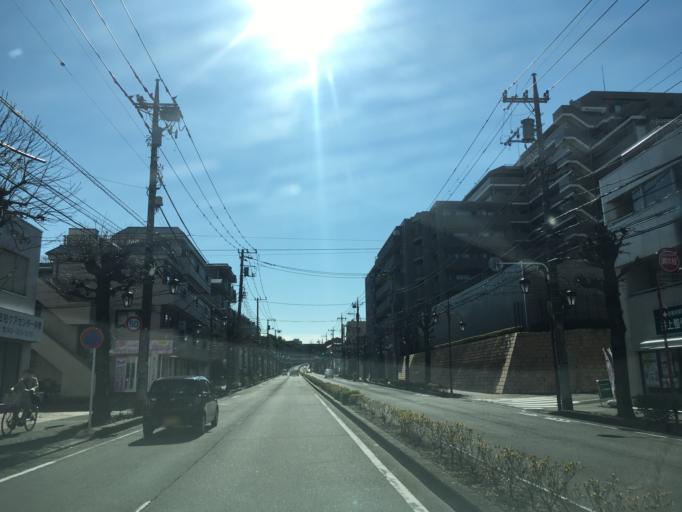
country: JP
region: Tokyo
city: Hino
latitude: 35.6254
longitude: 139.4308
